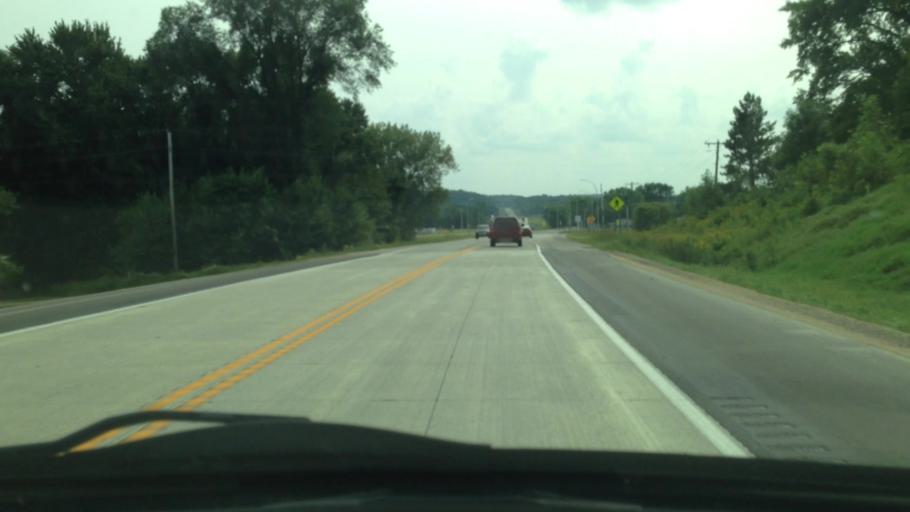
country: US
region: Minnesota
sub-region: Olmsted County
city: Rochester
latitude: 44.1109
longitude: -92.4294
